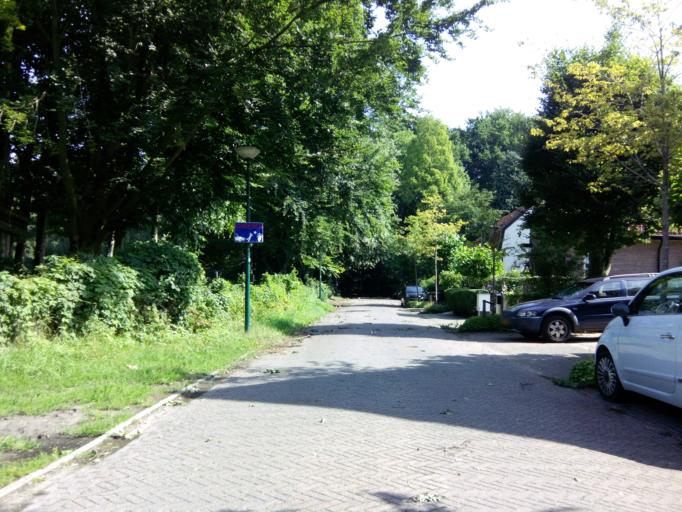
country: NL
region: Utrecht
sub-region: Gemeente Utrechtse Heuvelrug
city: Doorn
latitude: 52.0372
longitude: 5.3189
